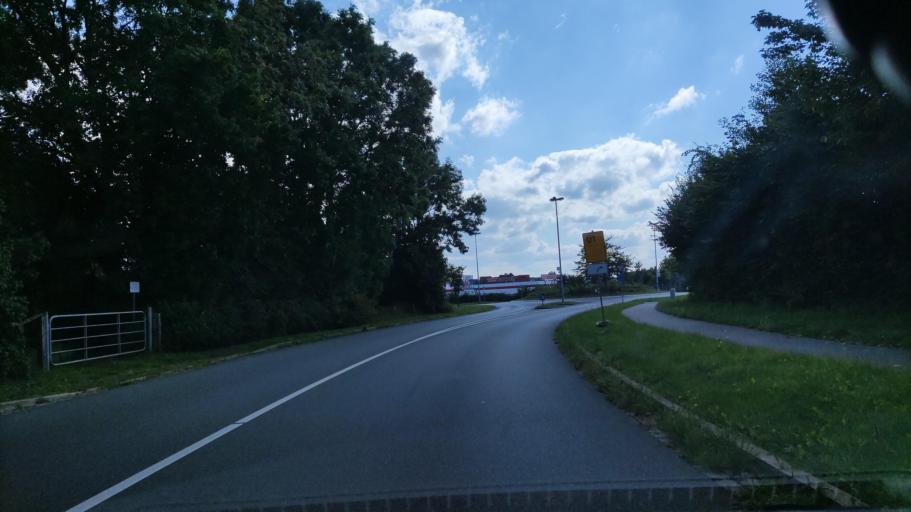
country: DE
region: Schleswig-Holstein
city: Rickert
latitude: 54.3259
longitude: 9.6303
